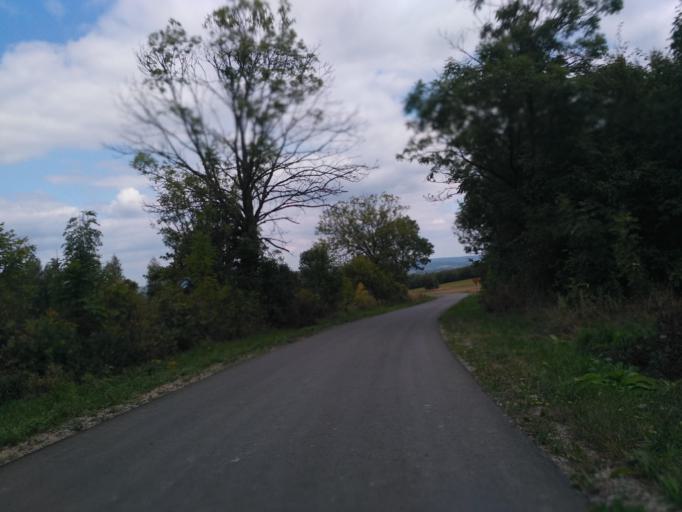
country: PL
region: Subcarpathian Voivodeship
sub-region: Powiat rzeszowski
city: Dynow
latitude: 49.7847
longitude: 22.2810
